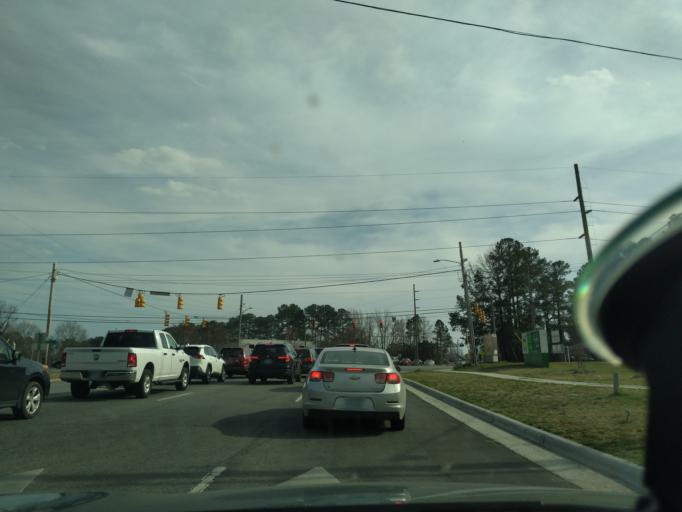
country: US
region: North Carolina
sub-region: Pitt County
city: Greenville
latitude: 35.5909
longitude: -77.3467
